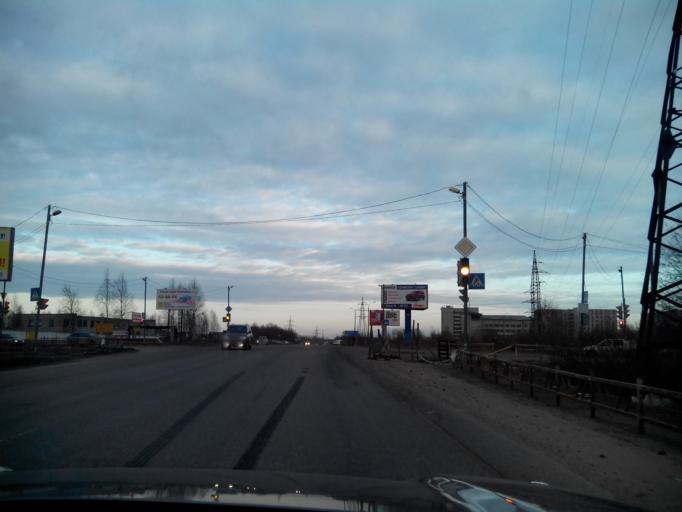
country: RU
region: Arkhangelskaya
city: Arkhangel'sk
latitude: 64.5194
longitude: 40.6760
